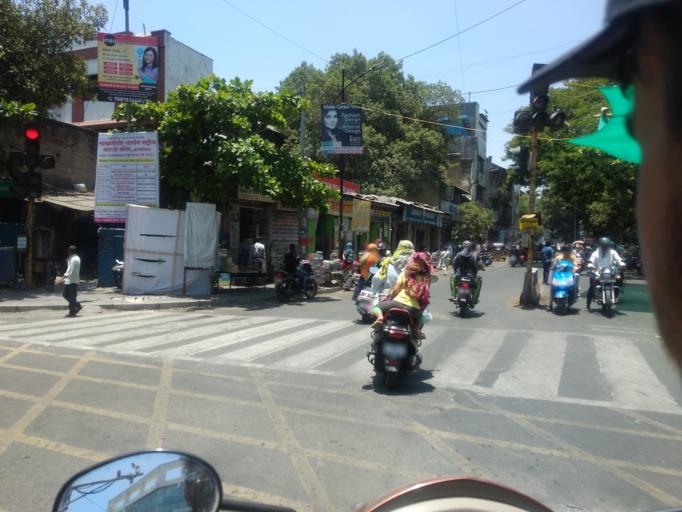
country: IN
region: Maharashtra
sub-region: Pune Division
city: Pune
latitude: 18.5165
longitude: 73.8537
